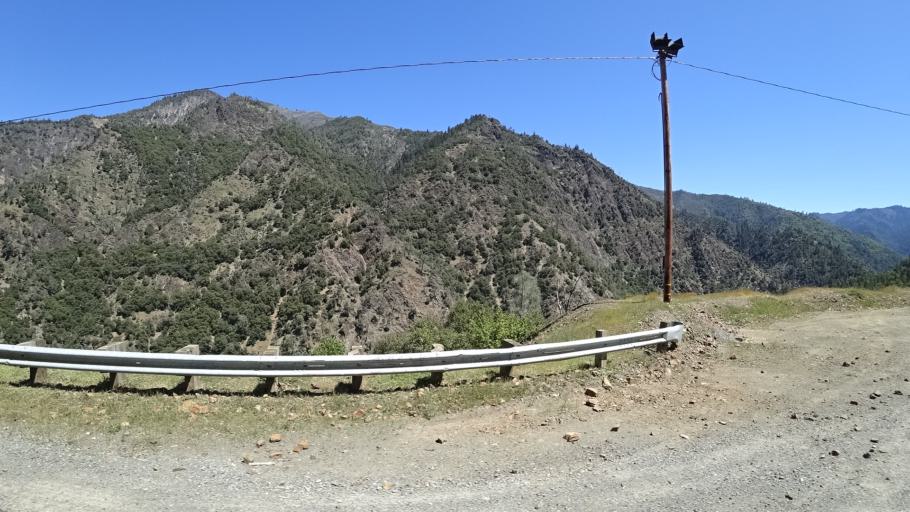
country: US
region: California
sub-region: Humboldt County
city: Willow Creek
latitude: 40.8153
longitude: -123.4780
